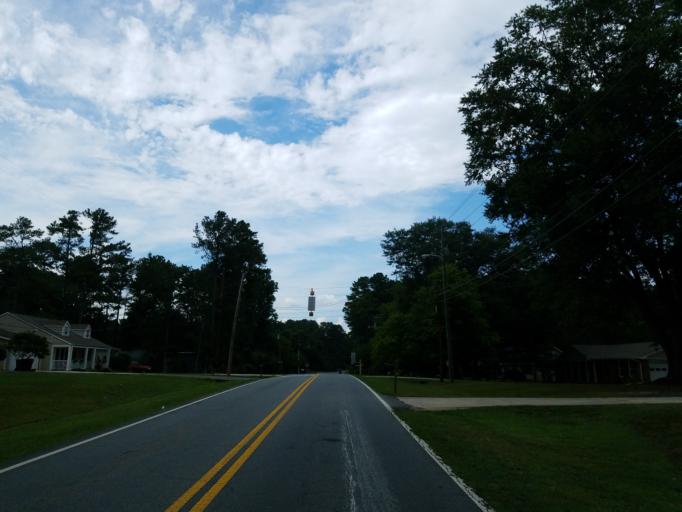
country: US
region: Georgia
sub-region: Cobb County
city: Smyrna
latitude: 33.9436
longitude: -84.4778
